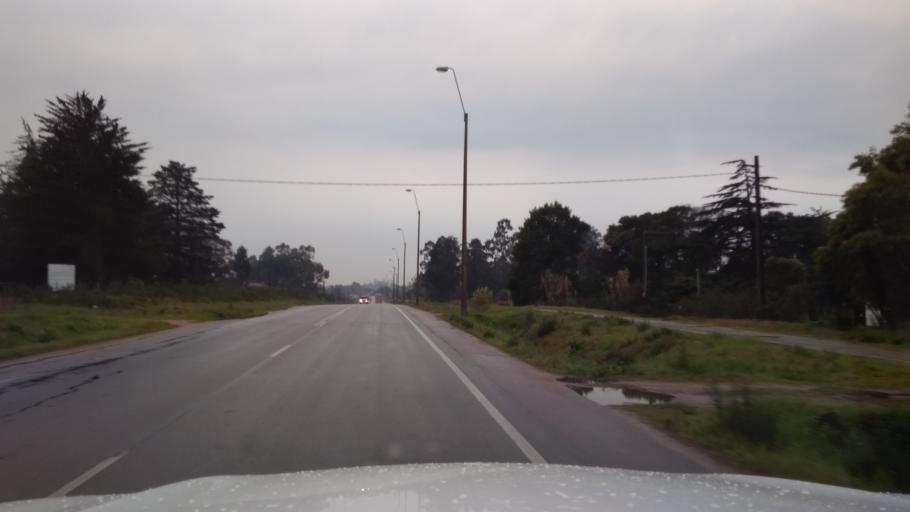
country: UY
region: Canelones
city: Toledo
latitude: -34.7614
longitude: -56.1163
